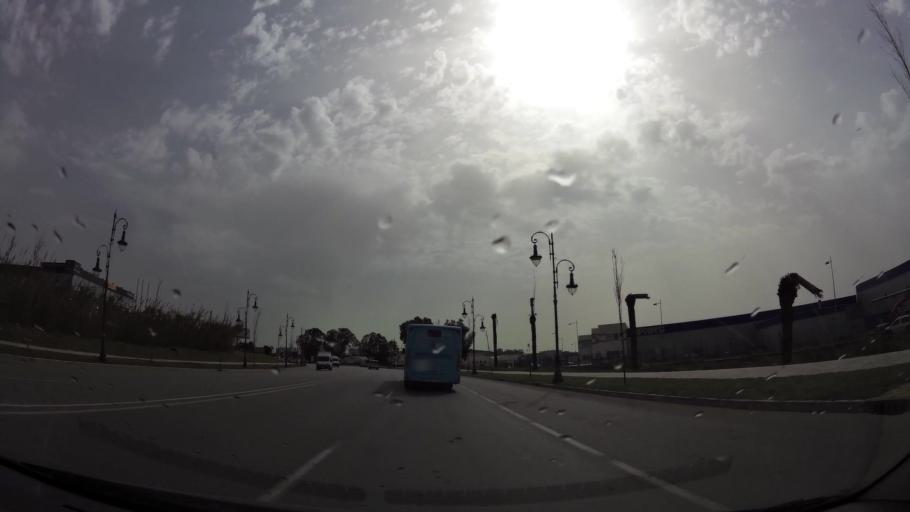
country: MA
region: Tanger-Tetouan
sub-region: Tanger-Assilah
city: Boukhalef
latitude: 35.7199
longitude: -5.9031
